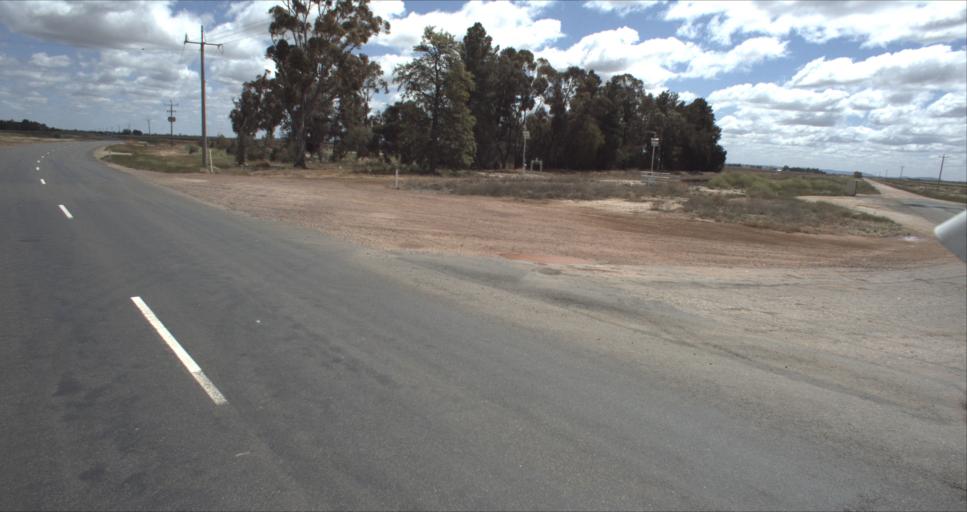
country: AU
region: New South Wales
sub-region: Murrumbidgee Shire
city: Darlington Point
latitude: -34.4689
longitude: 146.1364
